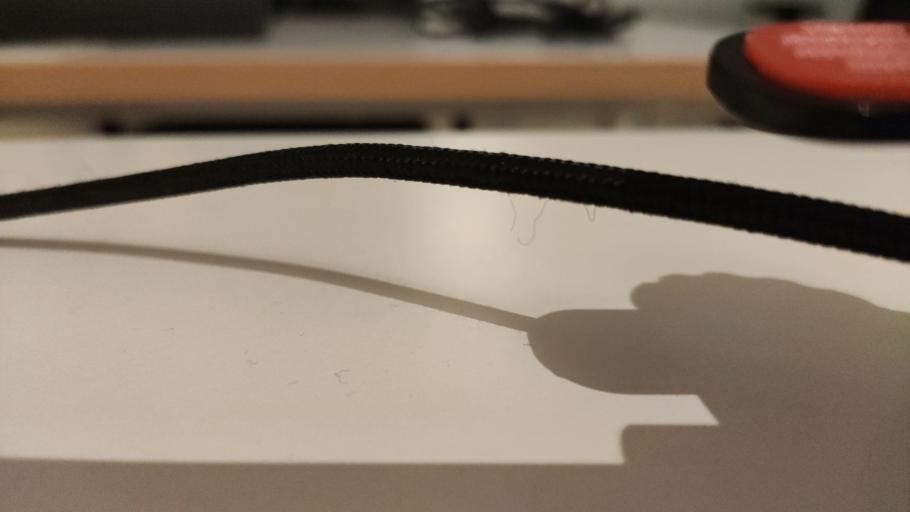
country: RU
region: Moskovskaya
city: Orekhovo-Zuyevo
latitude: 55.8332
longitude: 38.9674
